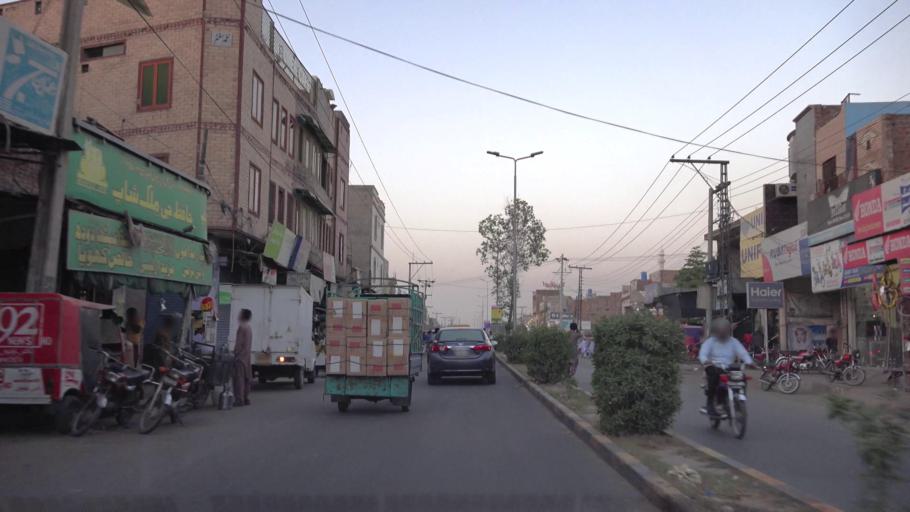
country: PK
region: Punjab
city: Faisalabad
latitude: 31.4463
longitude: 73.0963
